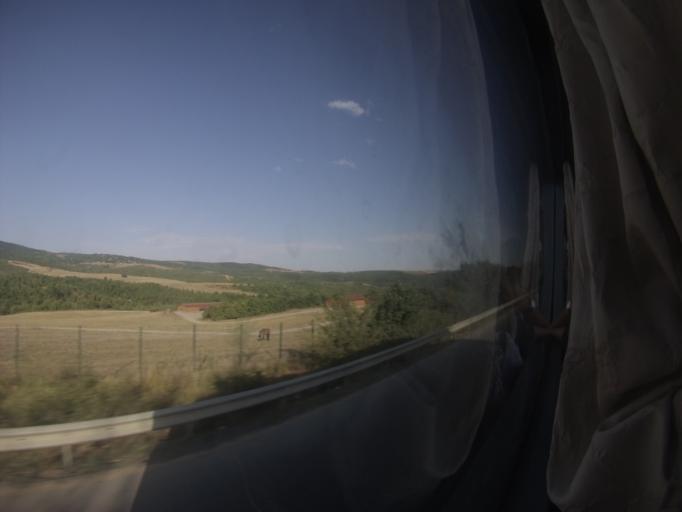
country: AZ
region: Ismayilli
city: Basqal
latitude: 40.7118
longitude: 48.3627
